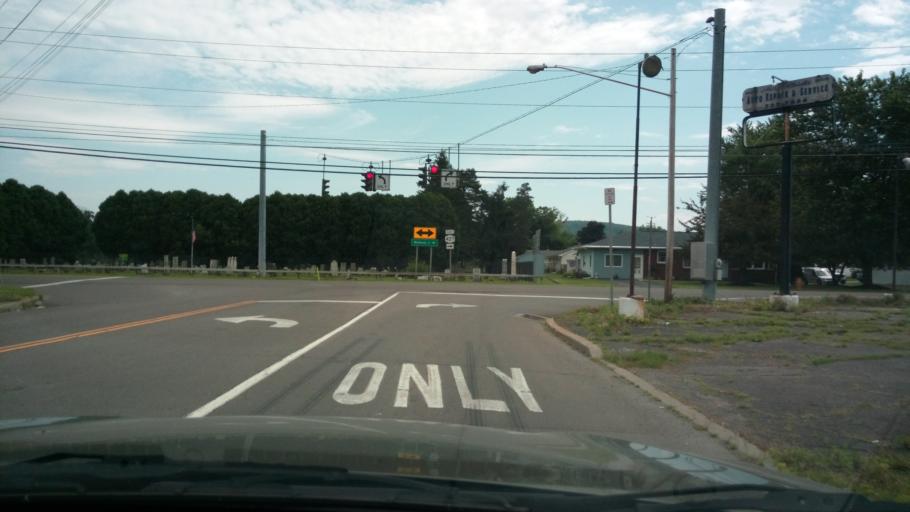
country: US
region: New York
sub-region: Chemung County
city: Southport
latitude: 42.0609
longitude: -76.7845
